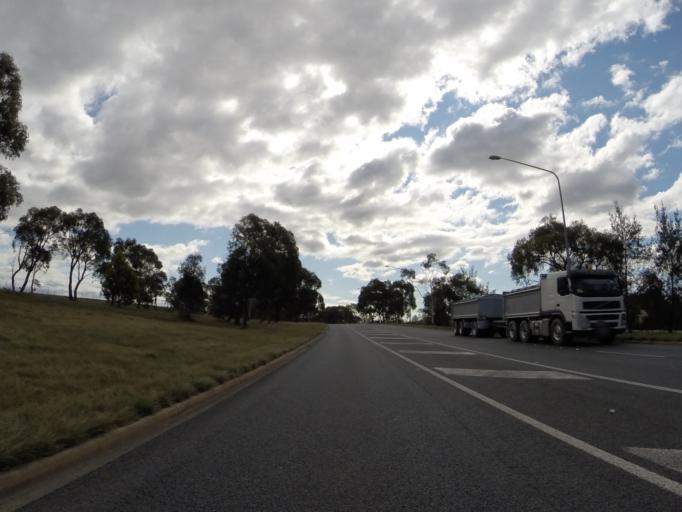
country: AU
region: Australian Capital Territory
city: Kaleen
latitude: -35.2179
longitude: 149.0955
